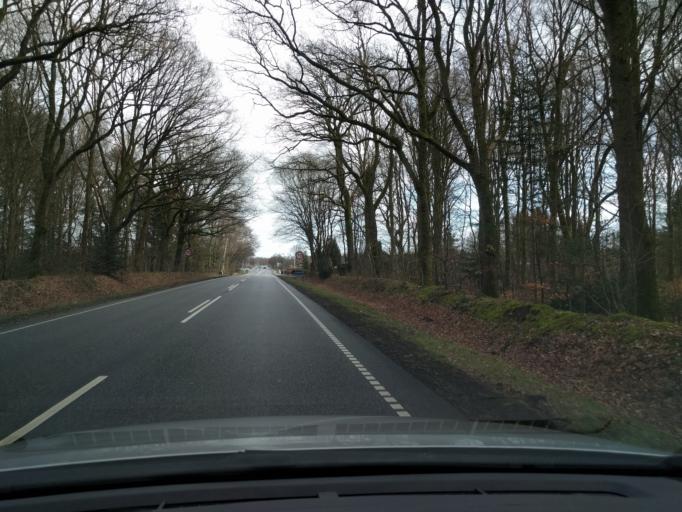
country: DK
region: South Denmark
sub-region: Tonder Kommune
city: Logumkloster
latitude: 55.0620
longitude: 8.9383
